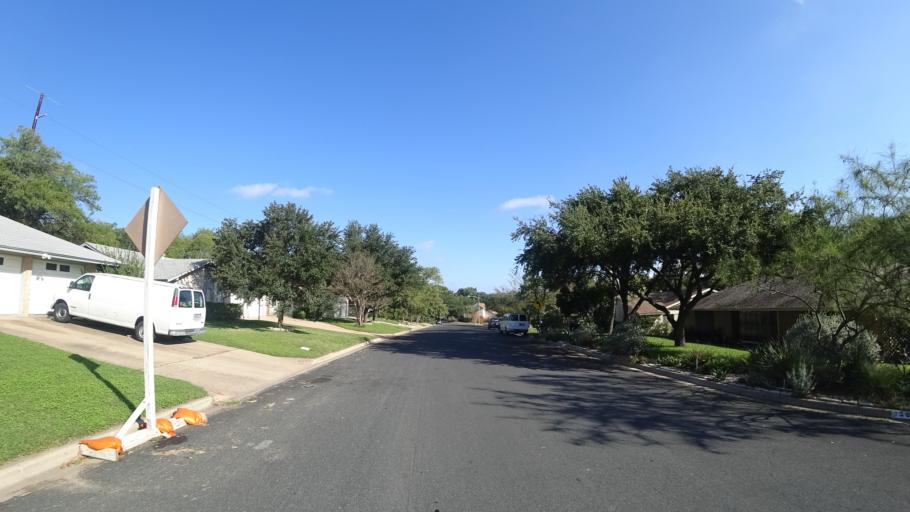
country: US
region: Texas
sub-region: Travis County
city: Austin
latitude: 30.3279
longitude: -97.6846
